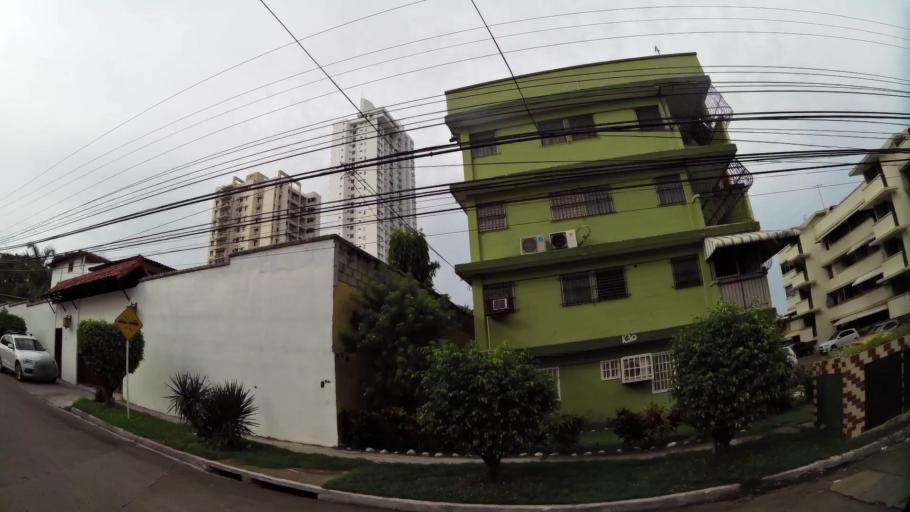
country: PA
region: Panama
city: Panama
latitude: 9.0085
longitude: -79.5118
